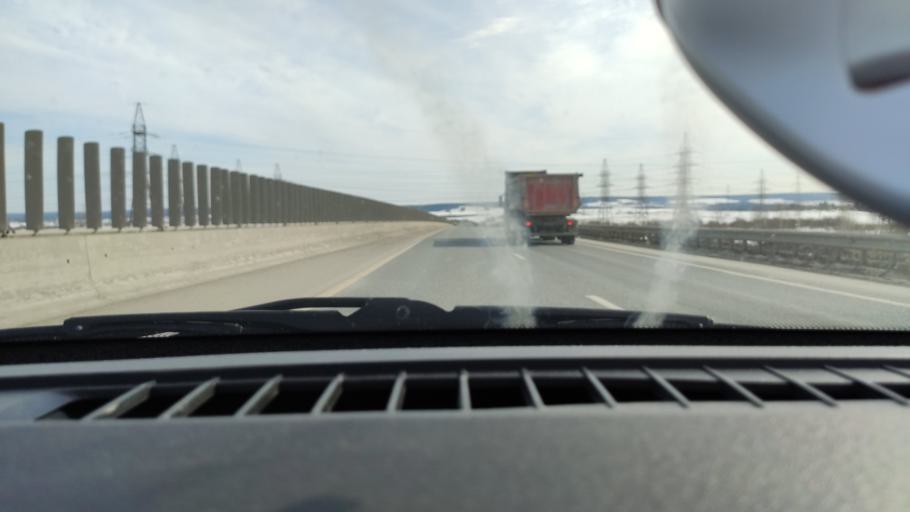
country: RU
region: Perm
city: Ferma
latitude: 57.9313
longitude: 56.3029
